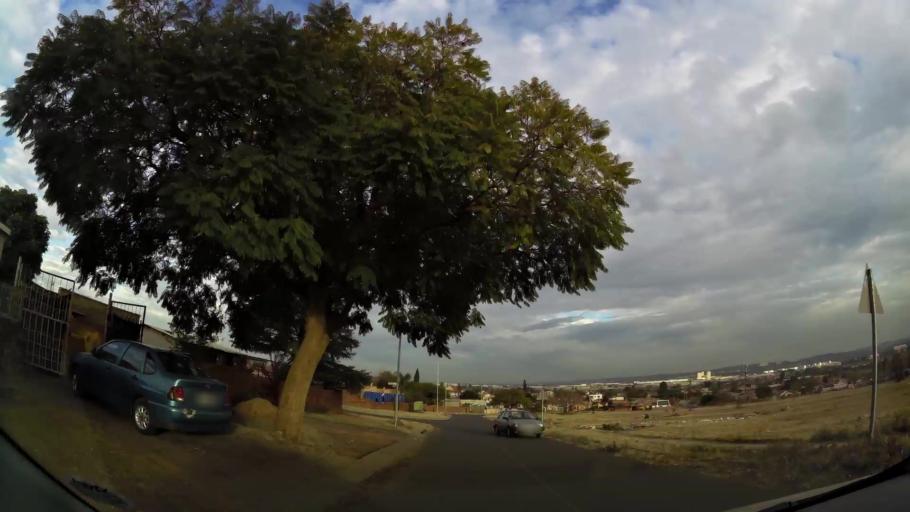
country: ZA
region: Gauteng
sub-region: City of Tshwane Metropolitan Municipality
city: Pretoria
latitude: -25.7007
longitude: 28.3199
